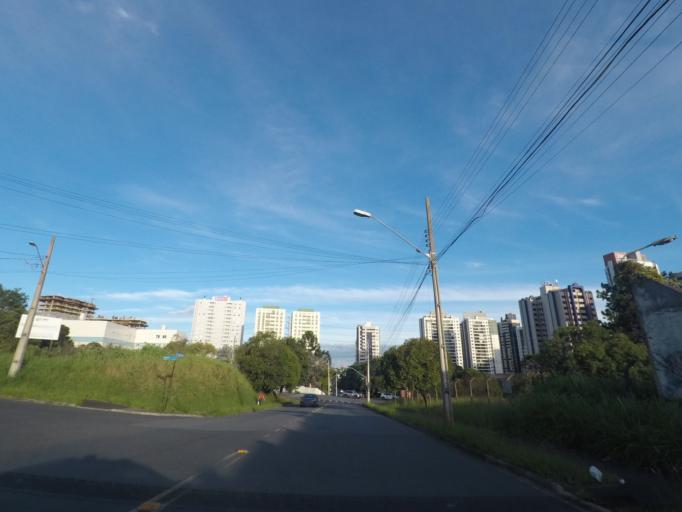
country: BR
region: Parana
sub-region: Curitiba
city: Curitiba
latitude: -25.4043
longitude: -49.2536
